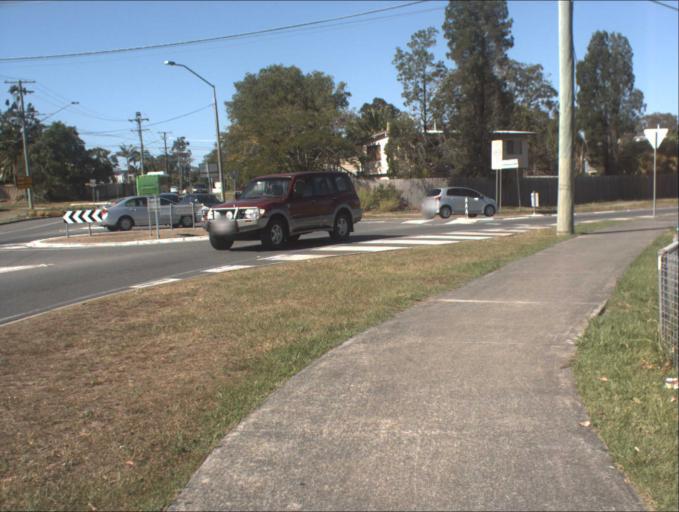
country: AU
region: Queensland
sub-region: Logan
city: Logan City
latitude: -27.6533
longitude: 153.0983
